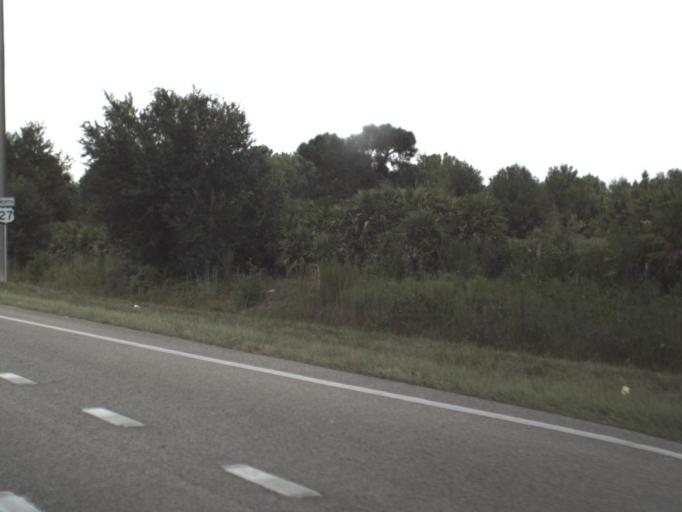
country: US
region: Florida
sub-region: Polk County
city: Frostproof
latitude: 27.7557
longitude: -81.5880
